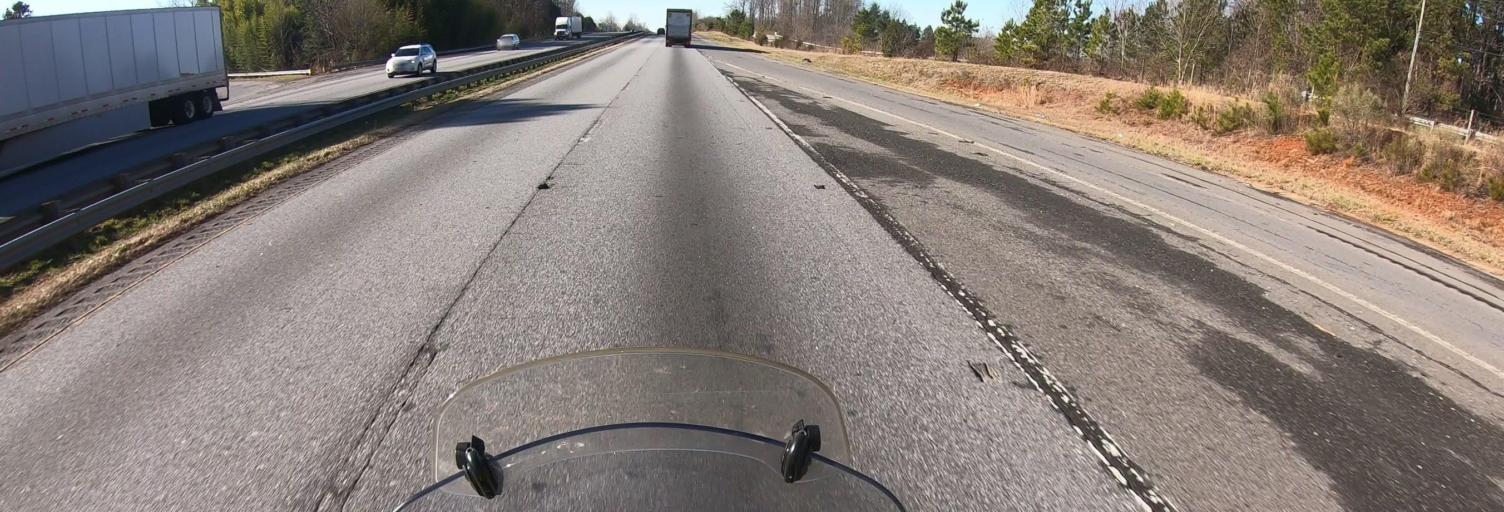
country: US
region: North Carolina
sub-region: Cleveland County
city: Kings Mountain
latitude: 35.2248
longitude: -81.3355
